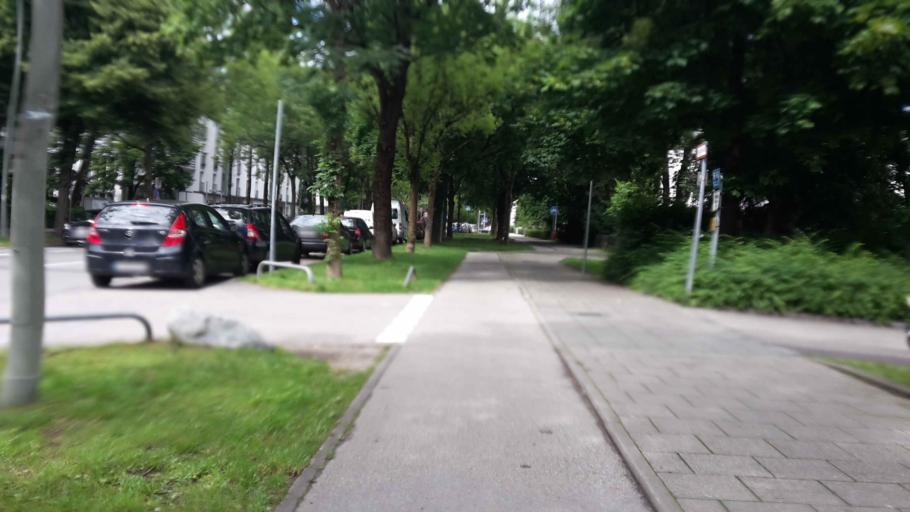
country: DE
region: Bavaria
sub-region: Upper Bavaria
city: Munich
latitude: 48.1064
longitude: 11.5639
